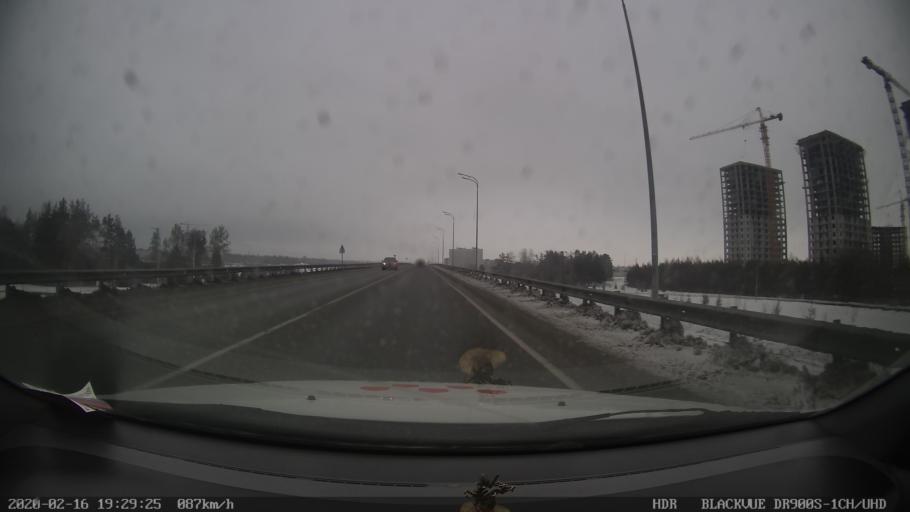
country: RU
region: Tatarstan
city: Stolbishchi
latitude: 55.6811
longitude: 49.1949
